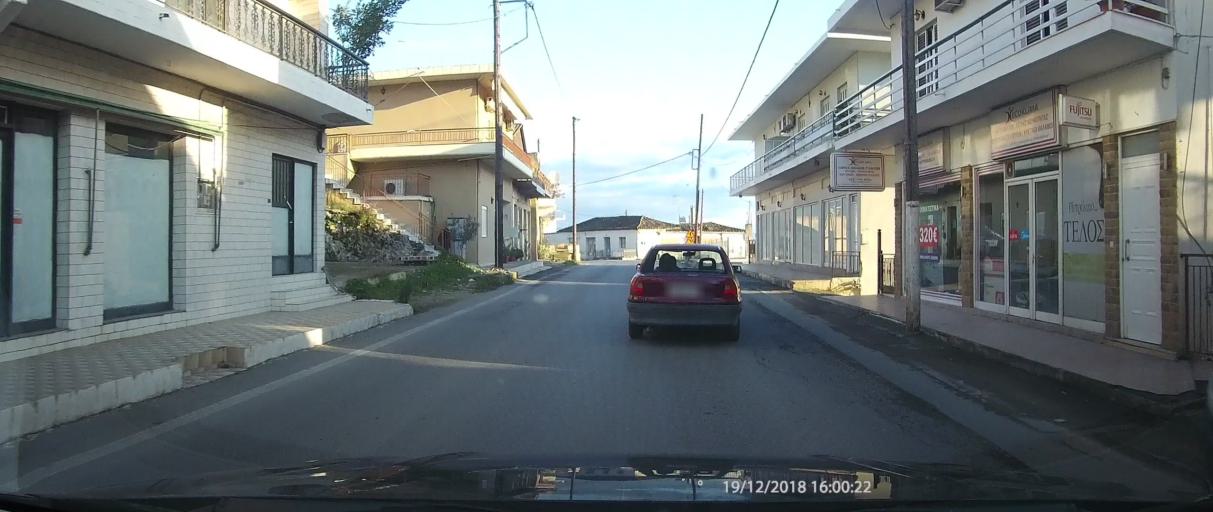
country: GR
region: Peloponnese
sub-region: Nomos Lakonias
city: Skala
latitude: 36.8547
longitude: 22.6776
